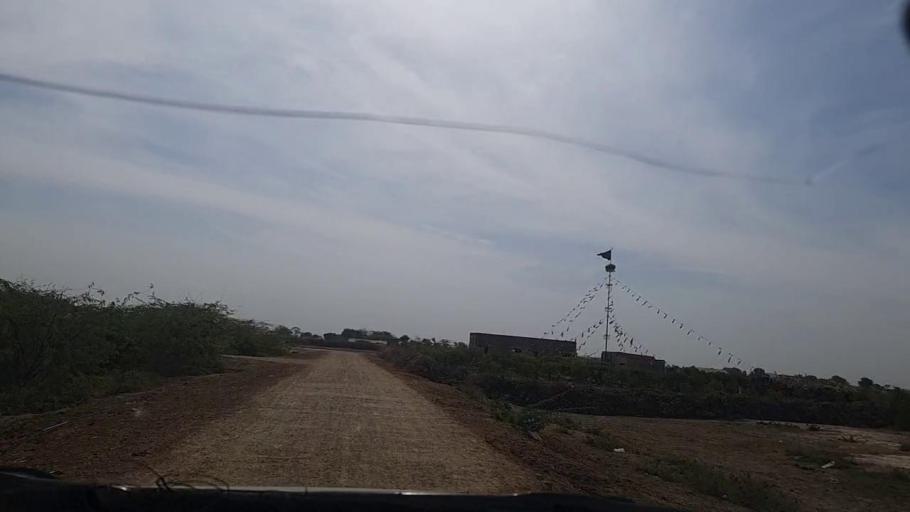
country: PK
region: Sindh
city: Dhoro Naro
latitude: 25.4363
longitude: 69.4974
